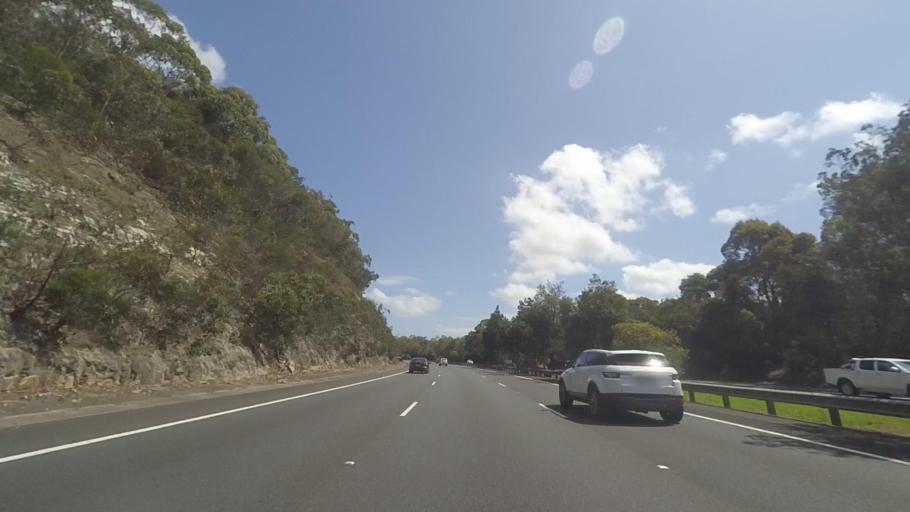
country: AU
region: New South Wales
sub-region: Ku-ring-gai
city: North Wahroonga
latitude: -33.6987
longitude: 151.1190
